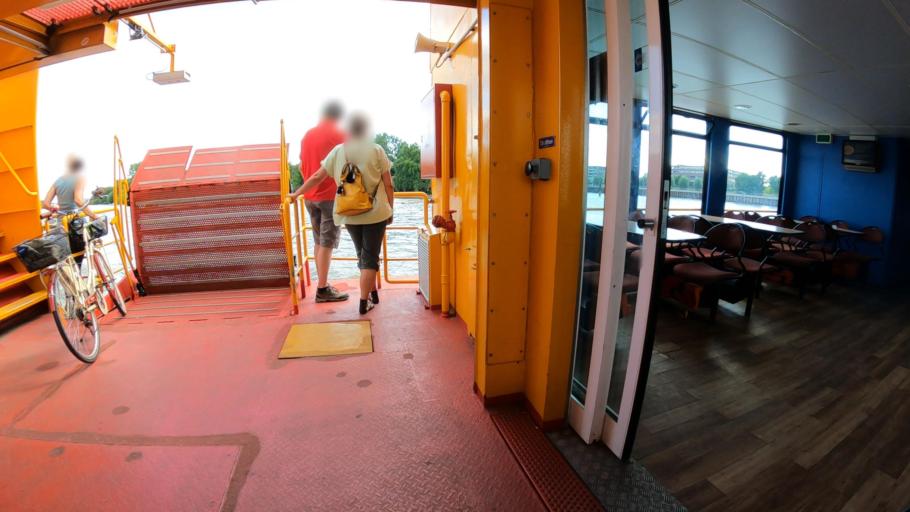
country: DE
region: Hamburg
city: Altona
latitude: 53.5420
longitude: 9.8684
